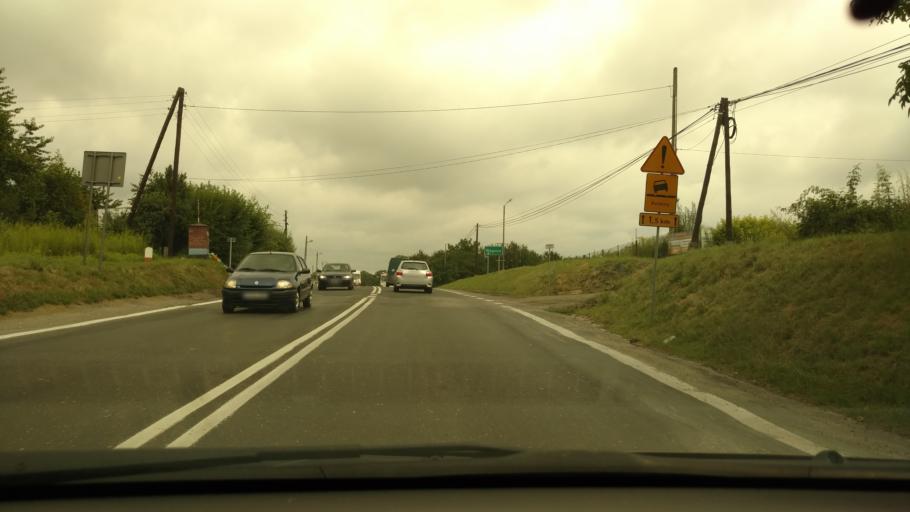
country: PL
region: Lesser Poland Voivodeship
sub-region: Powiat krakowski
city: Zielonki
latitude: 50.1090
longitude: 19.9657
